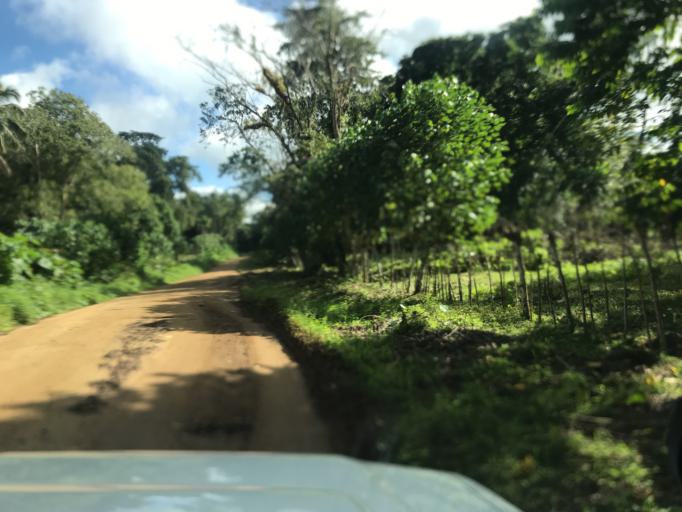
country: VU
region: Sanma
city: Luganville
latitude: -15.4989
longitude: 167.0913
